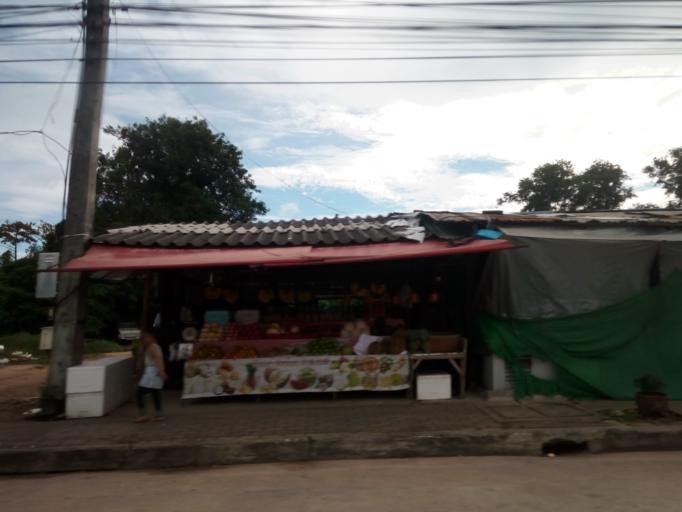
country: TH
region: Phuket
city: Ban Talat Nua
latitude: 7.8799
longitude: 98.3782
